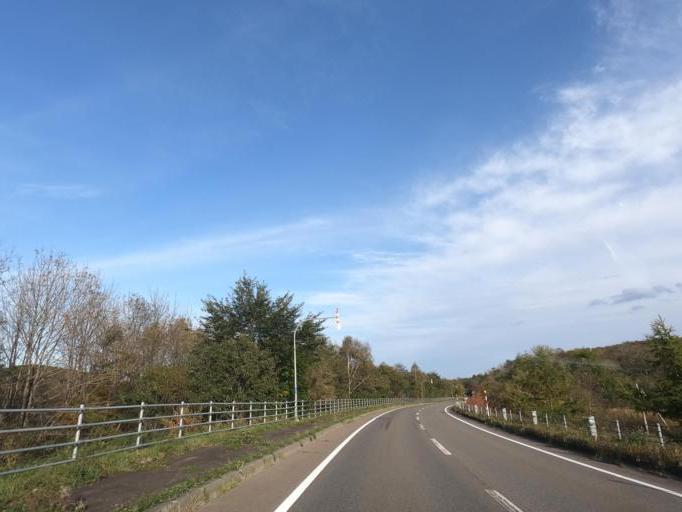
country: JP
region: Hokkaido
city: Obihiro
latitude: 42.5009
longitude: 143.4049
